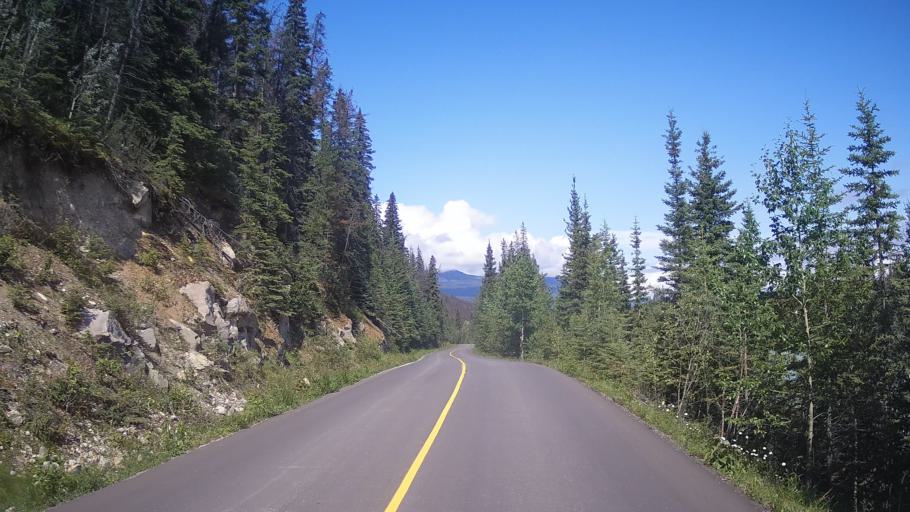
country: CA
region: Alberta
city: Jasper Park Lodge
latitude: 52.7398
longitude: -117.9608
